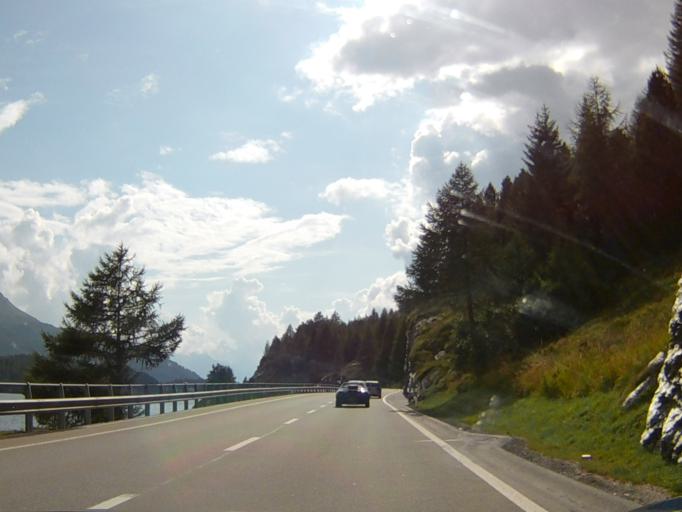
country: CH
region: Grisons
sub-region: Maloja District
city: Silvaplana
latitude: 46.4145
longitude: 9.7152
